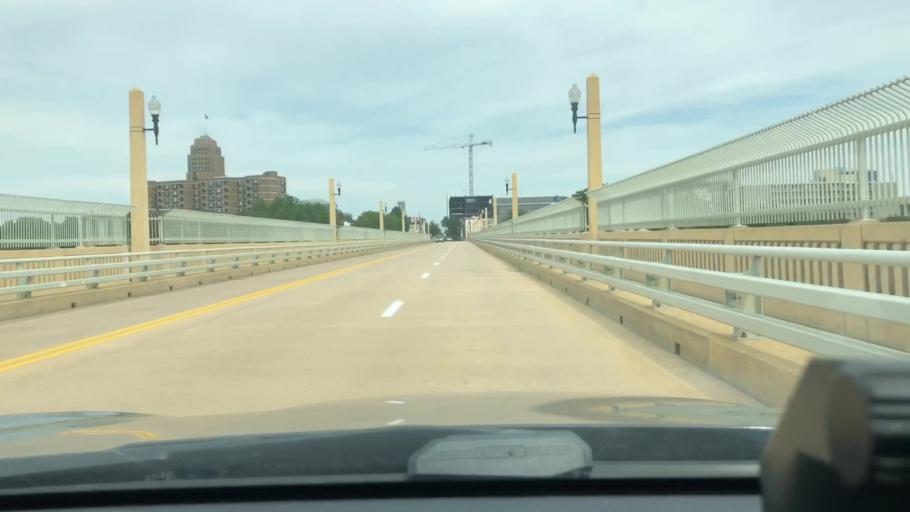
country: US
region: Pennsylvania
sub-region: Lehigh County
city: Allentown
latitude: 40.5957
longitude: -75.4708
